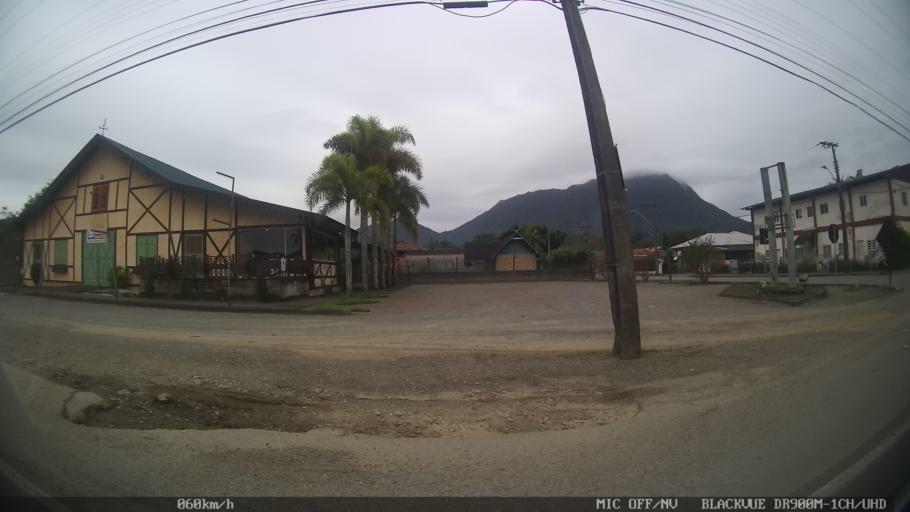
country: BR
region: Santa Catarina
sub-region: Joinville
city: Joinville
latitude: -26.1982
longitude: -48.9207
